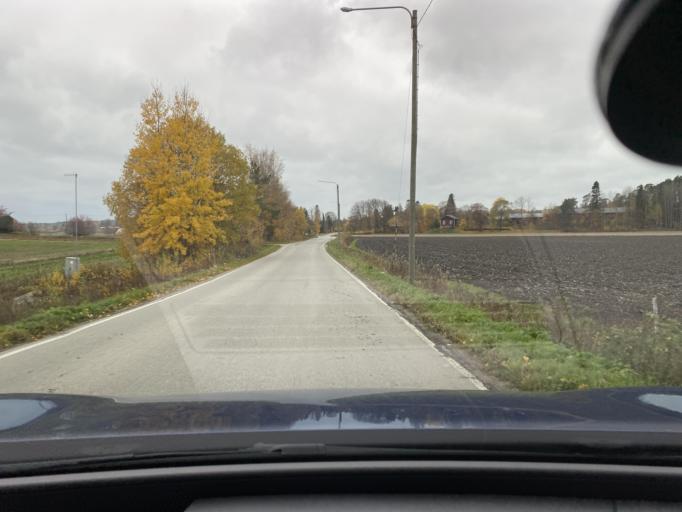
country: FI
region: Varsinais-Suomi
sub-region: Vakka-Suomi
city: Laitila
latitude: 60.9214
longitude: 21.5992
